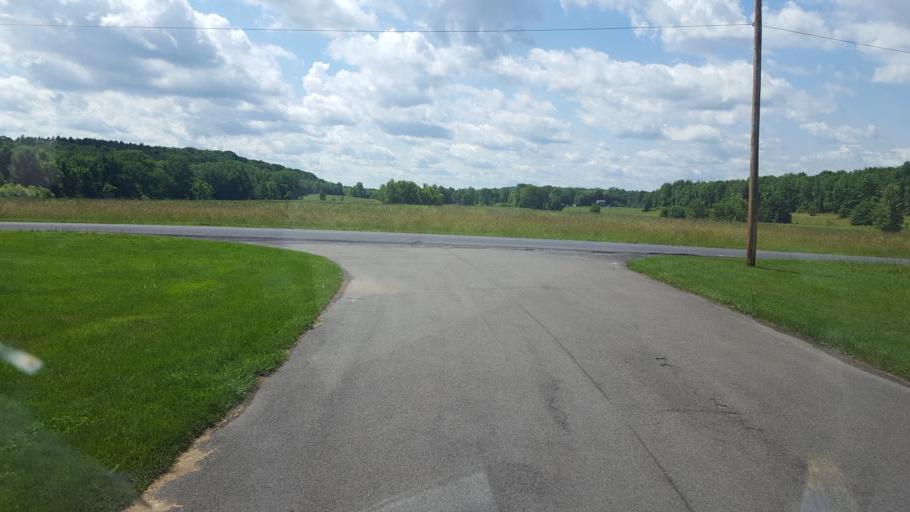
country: US
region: New York
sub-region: Wayne County
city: Wolcott
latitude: 43.2803
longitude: -76.9225
